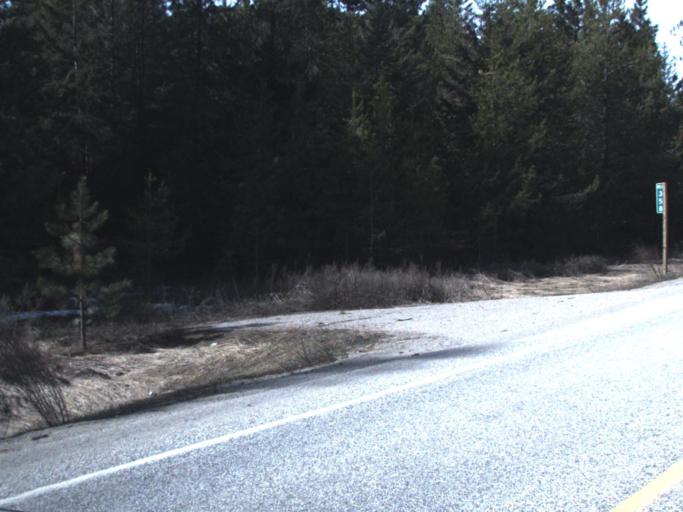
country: US
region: Washington
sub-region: Stevens County
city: Colville
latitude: 48.5402
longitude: -117.8308
